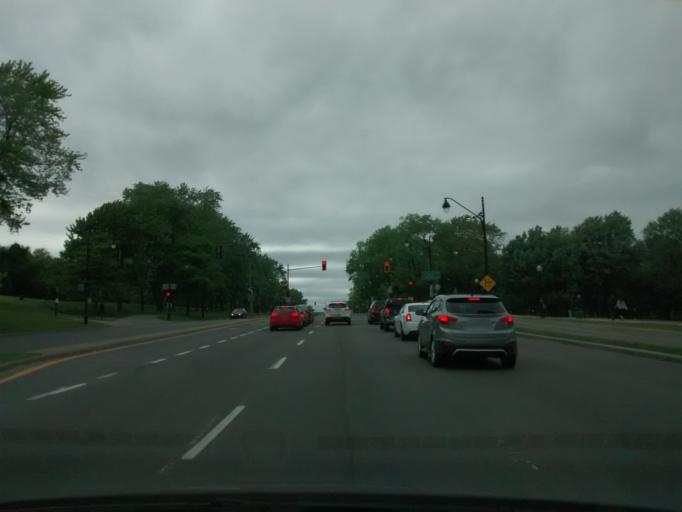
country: CA
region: Quebec
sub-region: Montreal
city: Montreal
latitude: 45.5131
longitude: -73.5812
